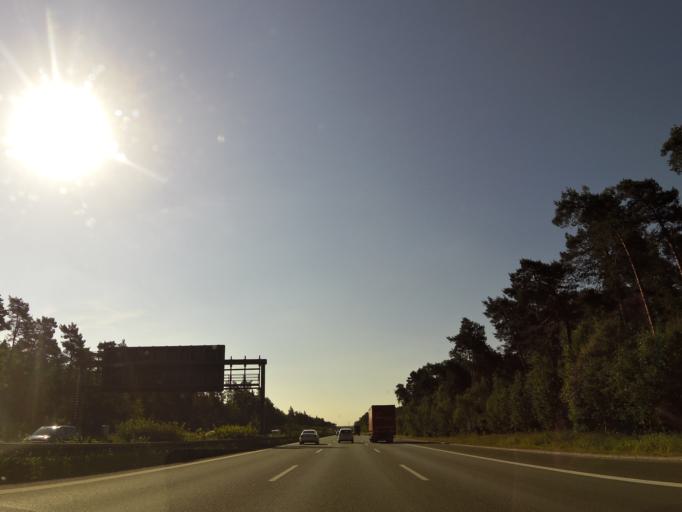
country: DE
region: Bavaria
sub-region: Regierungsbezirk Mittelfranken
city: Heroldsberg
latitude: 49.4931
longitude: 11.1486
